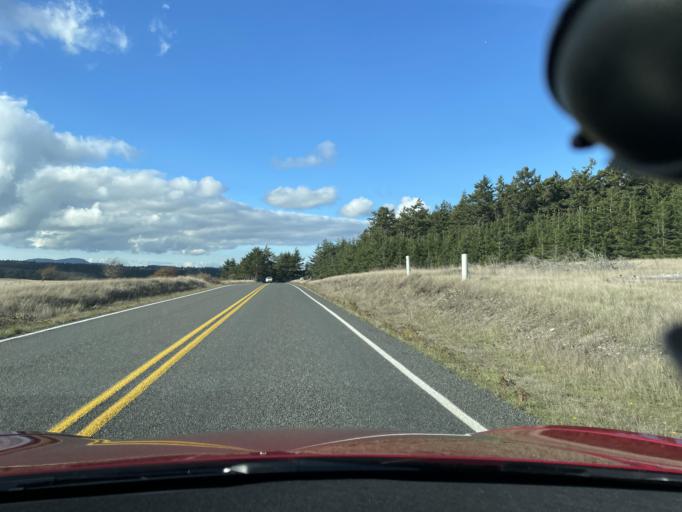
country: US
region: Washington
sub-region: San Juan County
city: Friday Harbor
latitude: 48.4614
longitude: -122.9967
